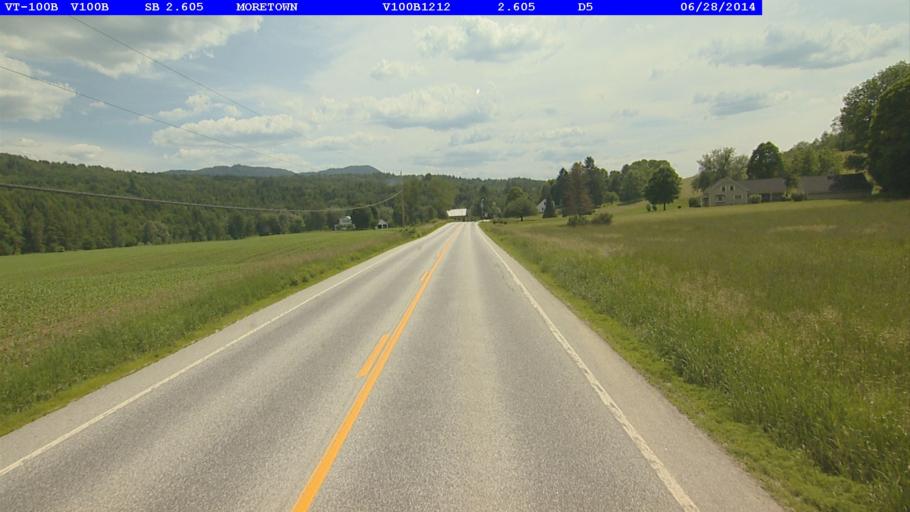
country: US
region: Vermont
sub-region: Washington County
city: Waterbury
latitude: 44.2668
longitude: -72.7467
